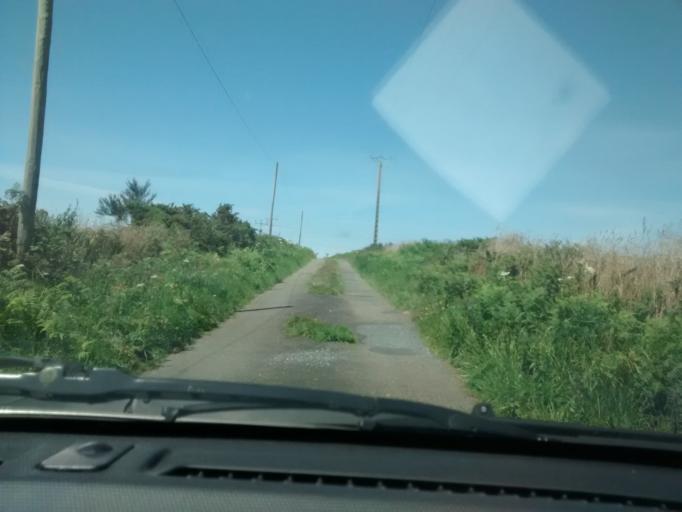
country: FR
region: Brittany
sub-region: Departement des Cotes-d'Armor
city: Trevou-Treguignec
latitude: 48.7817
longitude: -3.3322
